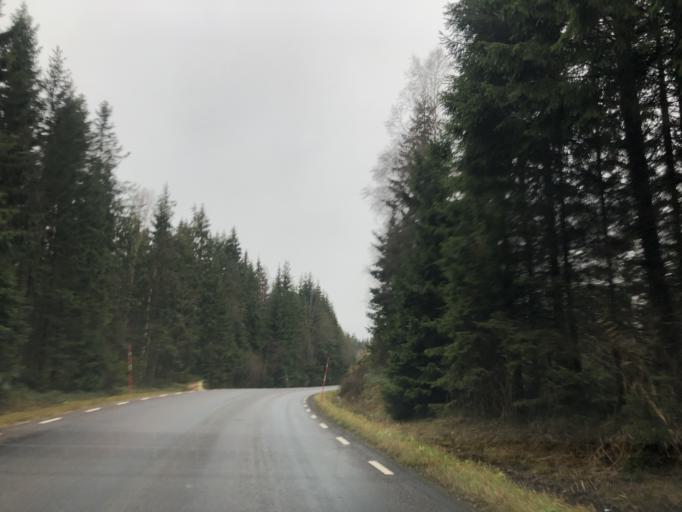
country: SE
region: Vaestra Goetaland
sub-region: Ulricehamns Kommun
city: Ulricehamn
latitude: 57.7044
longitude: 13.5694
